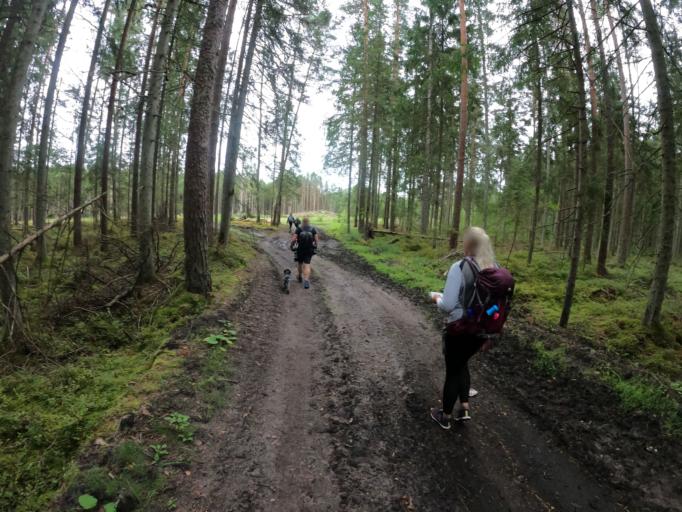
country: LV
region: Kuldigas Rajons
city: Kuldiga
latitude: 57.0409
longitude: 22.0655
